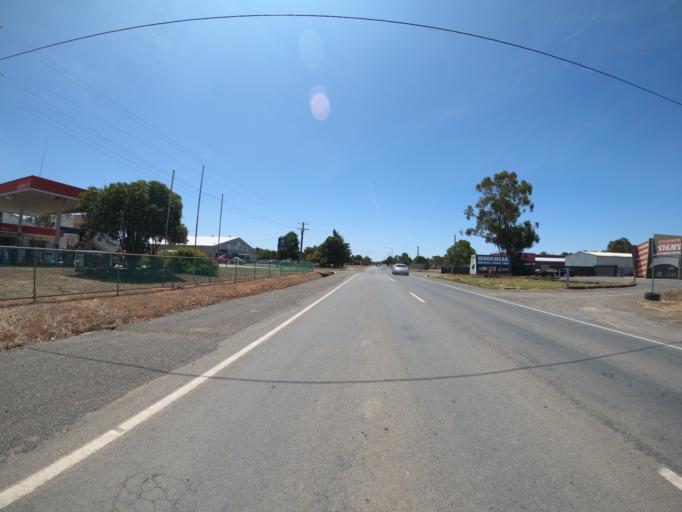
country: AU
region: Victoria
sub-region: Moira
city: Yarrawonga
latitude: -36.0294
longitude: 145.9955
